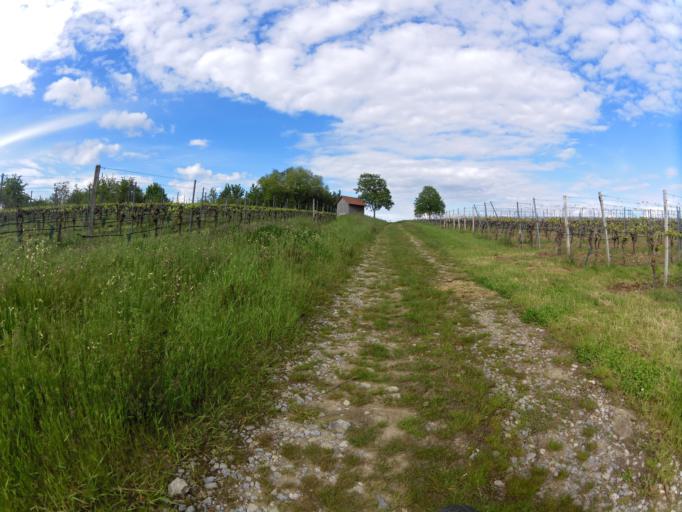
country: DE
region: Bavaria
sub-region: Regierungsbezirk Unterfranken
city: Sommerach
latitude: 49.8411
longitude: 10.1899
